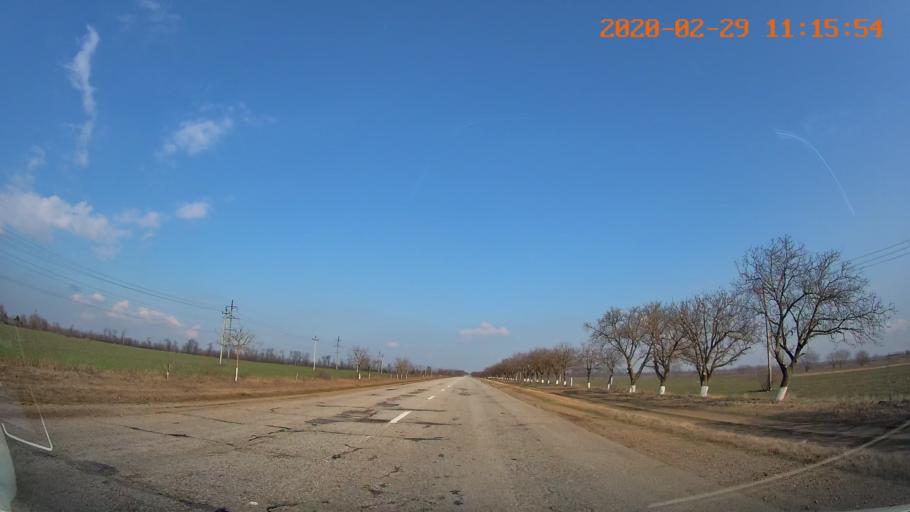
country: MD
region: Telenesti
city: Dubasari
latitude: 47.3009
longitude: 29.1663
